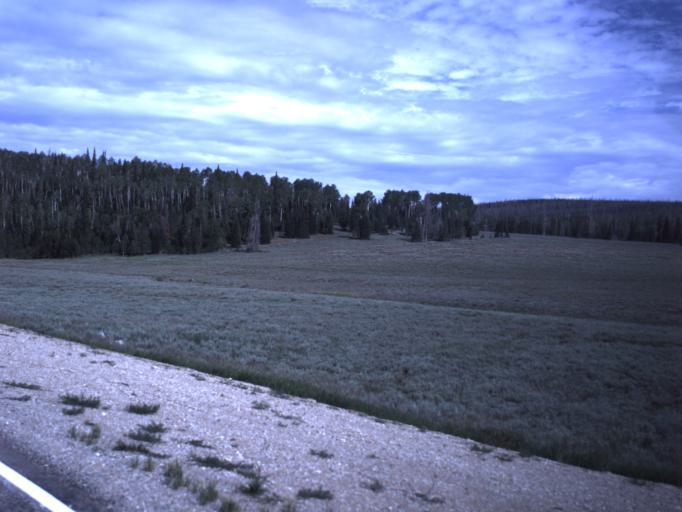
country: US
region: Utah
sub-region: Iron County
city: Parowan
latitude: 37.5691
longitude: -112.7955
